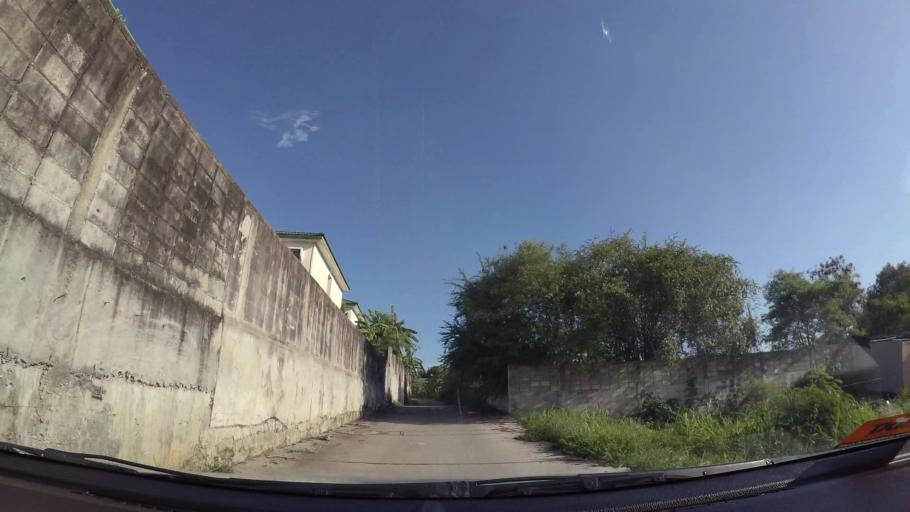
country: TH
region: Chon Buri
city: Si Racha
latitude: 13.1488
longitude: 100.9375
